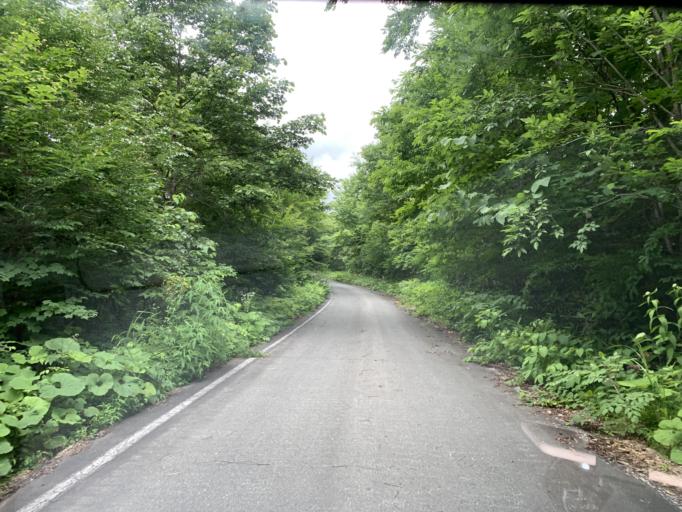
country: JP
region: Iwate
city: Ichinoseki
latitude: 38.9318
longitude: 140.8864
